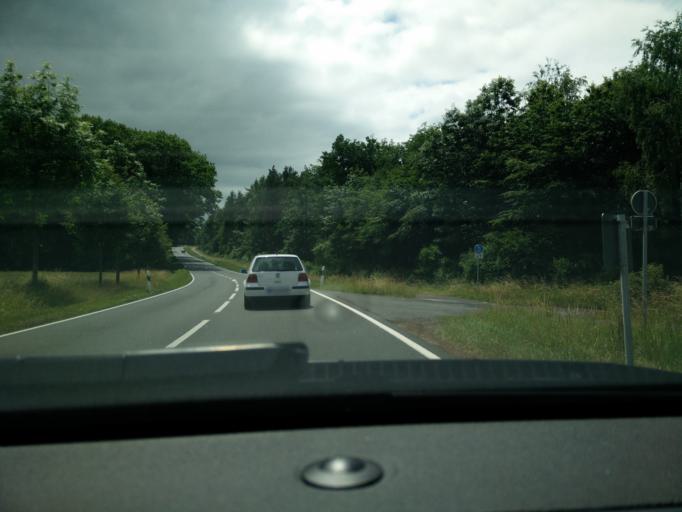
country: DE
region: Saxony
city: Grossbardau
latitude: 51.1734
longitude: 12.6812
